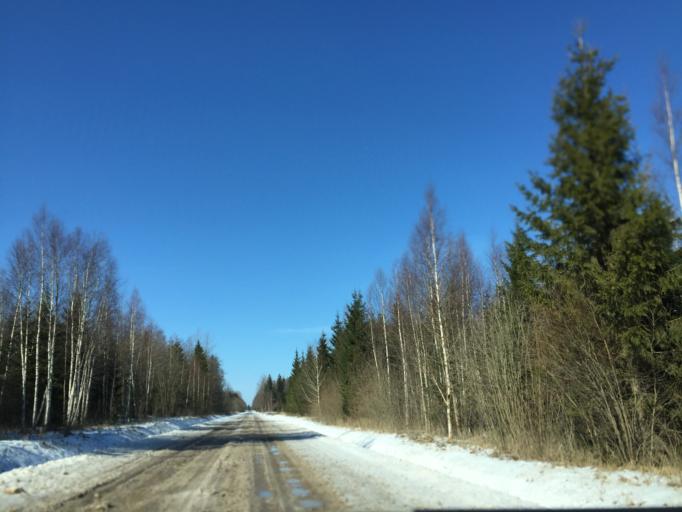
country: LV
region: Salacgrivas
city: Ainazi
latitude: 58.0298
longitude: 24.5210
